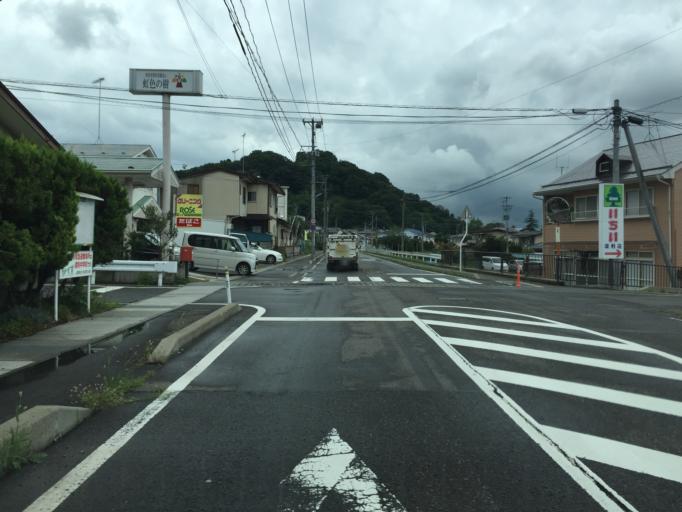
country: JP
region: Fukushima
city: Fukushima-shi
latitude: 37.7424
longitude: 140.4807
